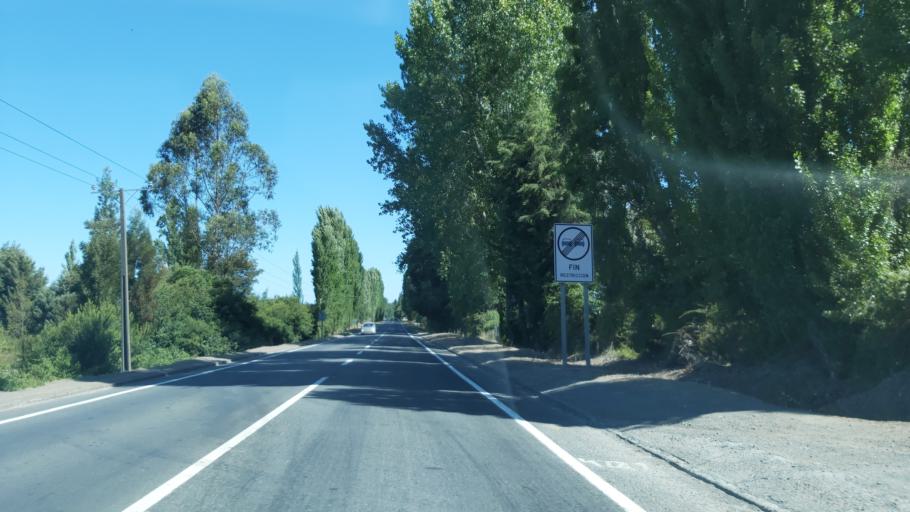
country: CL
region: Biobio
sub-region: Provincia de Concepcion
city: Lota
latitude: -37.1428
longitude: -72.9781
